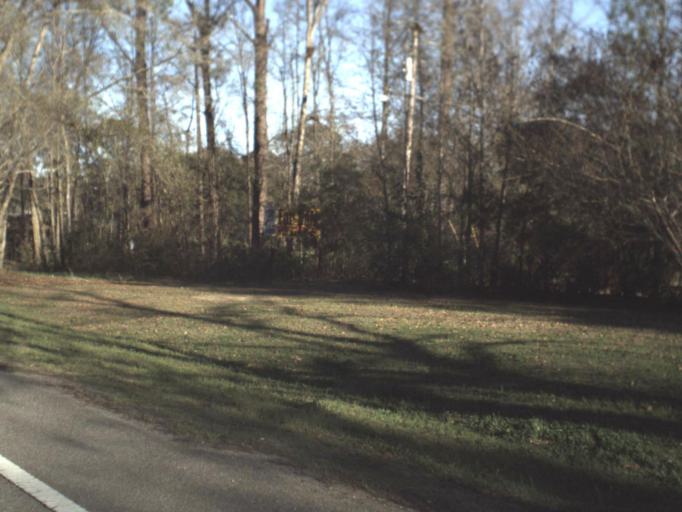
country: US
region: Florida
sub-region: Leon County
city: Tallahassee
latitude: 30.4911
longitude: -84.1280
